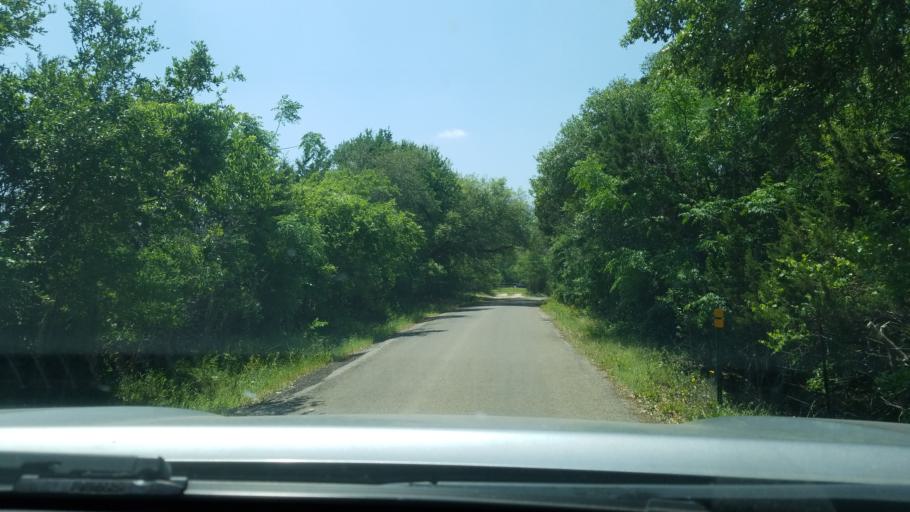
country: US
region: Texas
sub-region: Blanco County
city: Blanco
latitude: 30.0011
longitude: -98.4105
